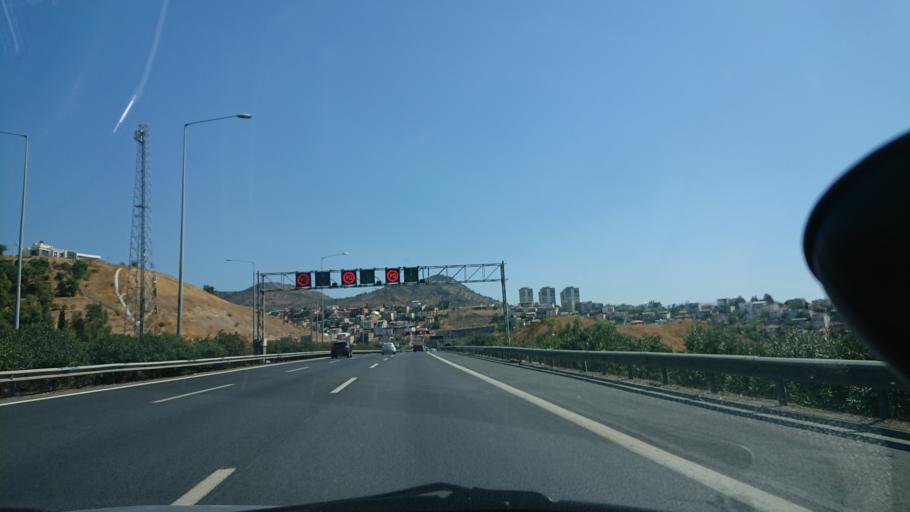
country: TR
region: Izmir
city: Karsiyaka
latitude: 38.4862
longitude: 27.1312
